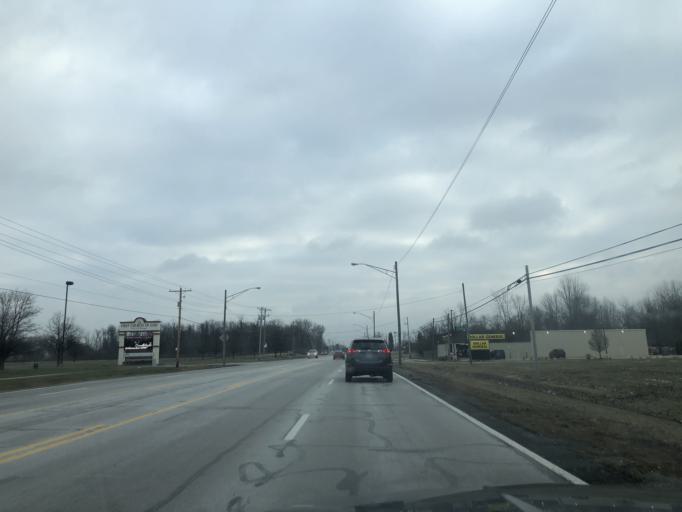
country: US
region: Ohio
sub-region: Franklin County
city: Groveport
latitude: 39.9170
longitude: -82.9098
